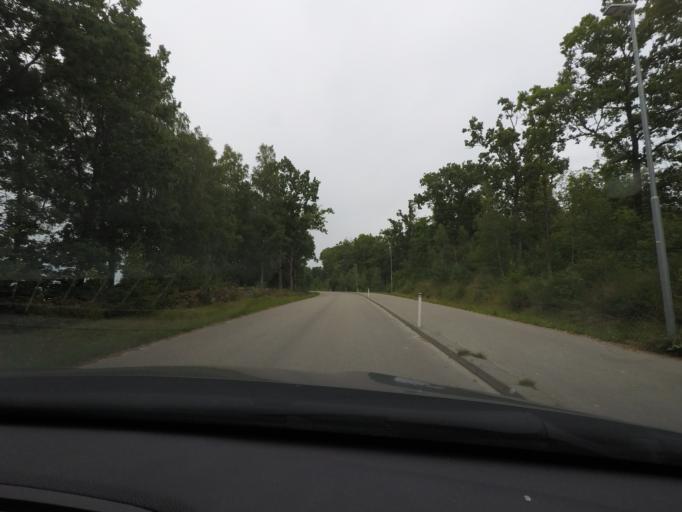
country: SE
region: Skane
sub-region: Osby Kommun
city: Osby
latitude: 56.3633
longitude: 14.0009
